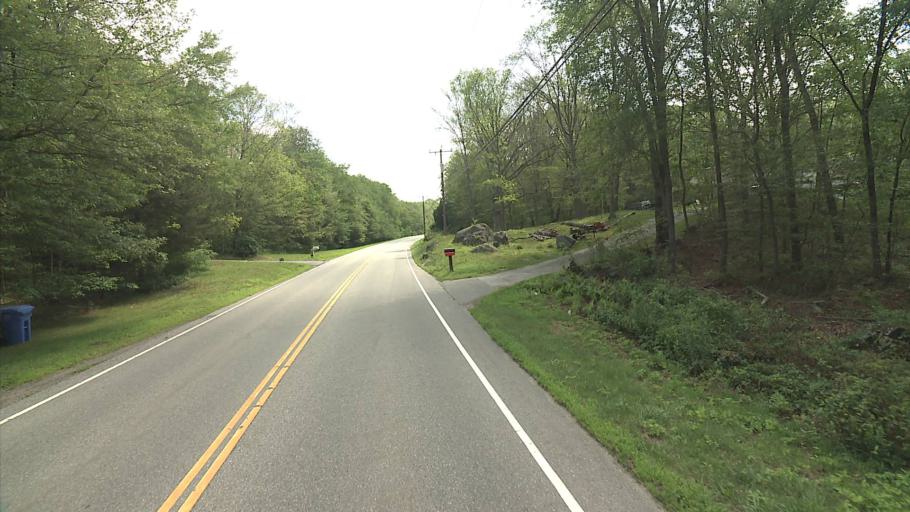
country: US
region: Connecticut
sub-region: New London County
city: Preston City
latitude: 41.5347
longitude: -71.9365
